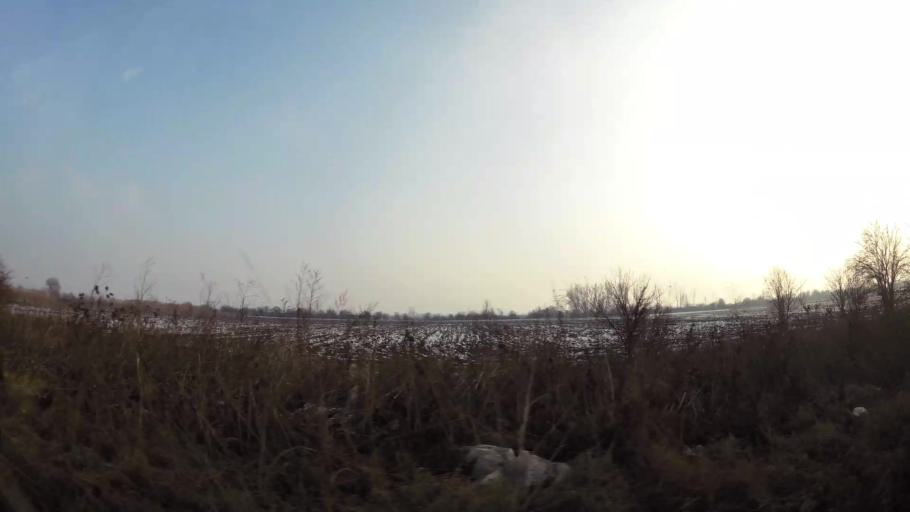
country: MK
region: Aracinovo
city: Arachinovo
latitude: 42.0209
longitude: 21.5427
